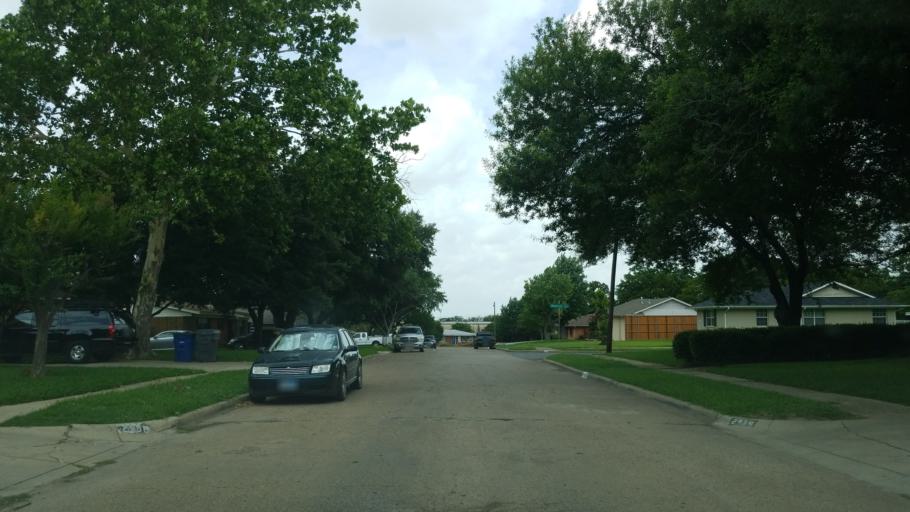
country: US
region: Texas
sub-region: Dallas County
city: Farmers Branch
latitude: 32.8879
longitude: -96.8801
